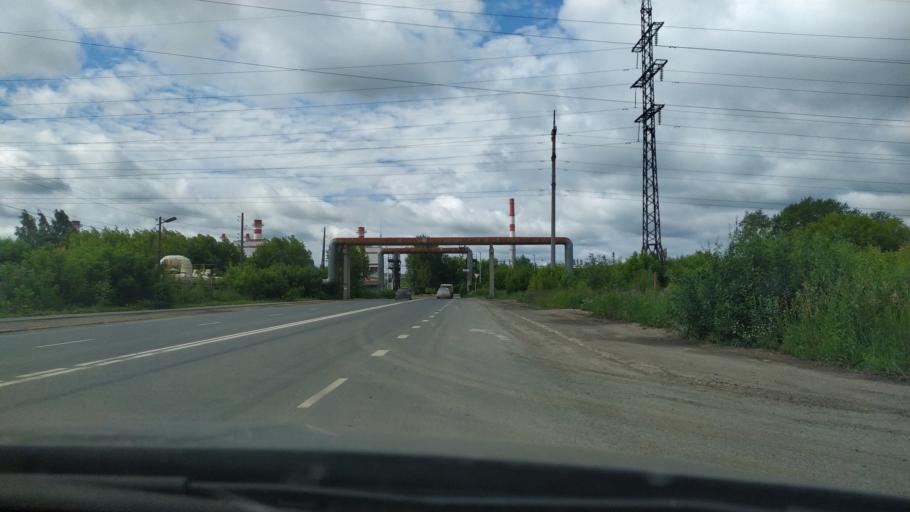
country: RU
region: Perm
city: Kondratovo
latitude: 57.9267
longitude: 56.1383
